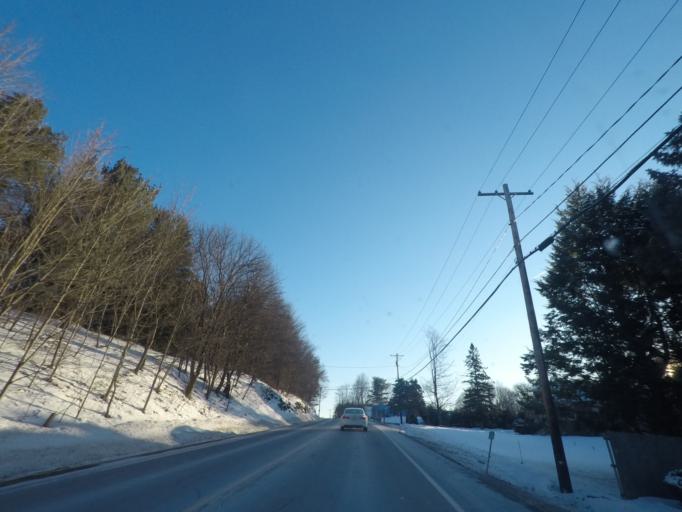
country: US
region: New York
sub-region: Saratoga County
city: Waterford
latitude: 42.8239
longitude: -73.6302
